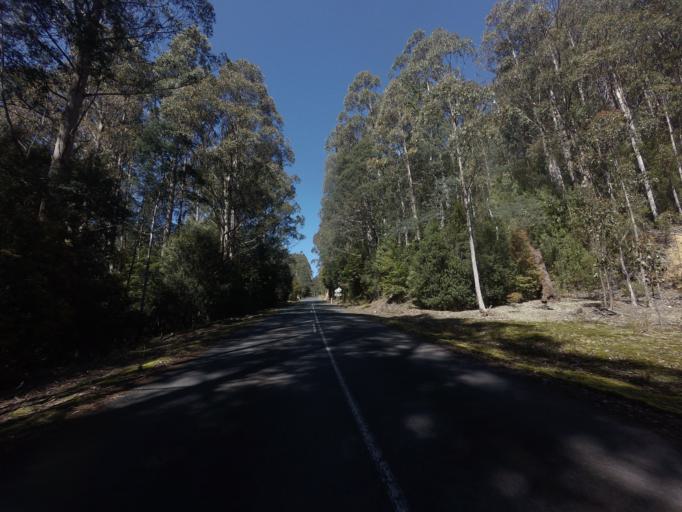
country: AU
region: Tasmania
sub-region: Huon Valley
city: Geeveston
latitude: -42.8163
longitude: 146.3471
